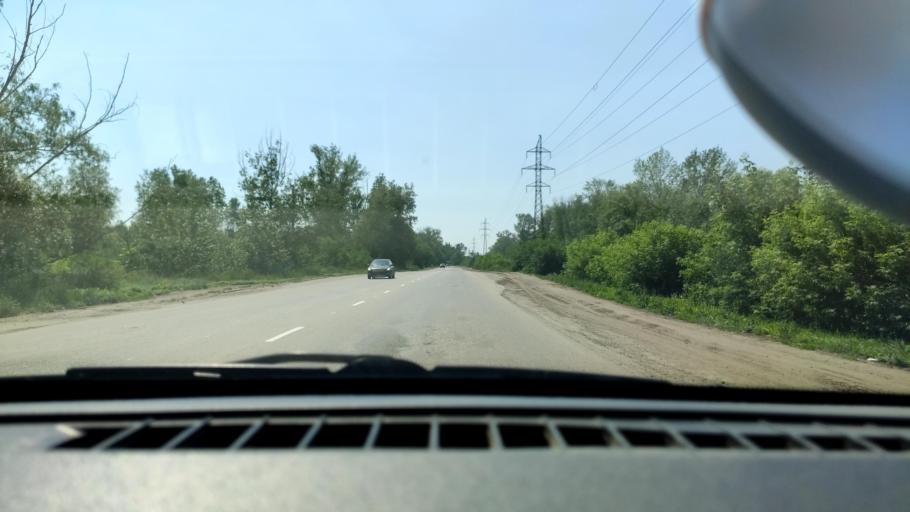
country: RU
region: Samara
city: Rozhdestveno
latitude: 53.1396
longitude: 50.0604
